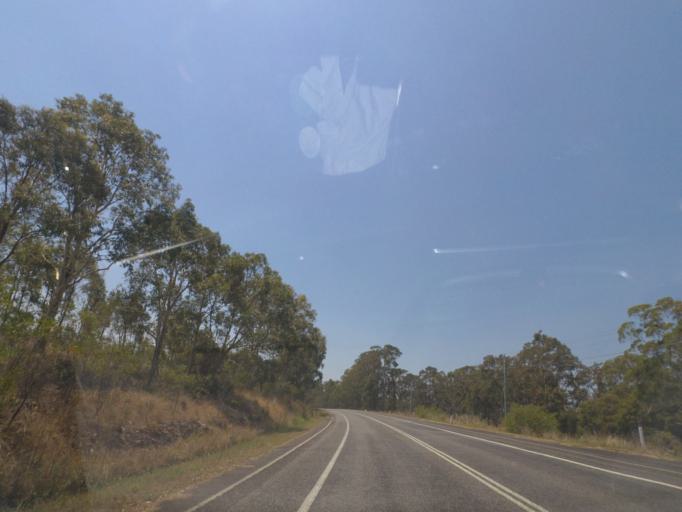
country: AU
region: New South Wales
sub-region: Port Stephens Shire
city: Port Stephens
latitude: -32.6332
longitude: 152.0469
